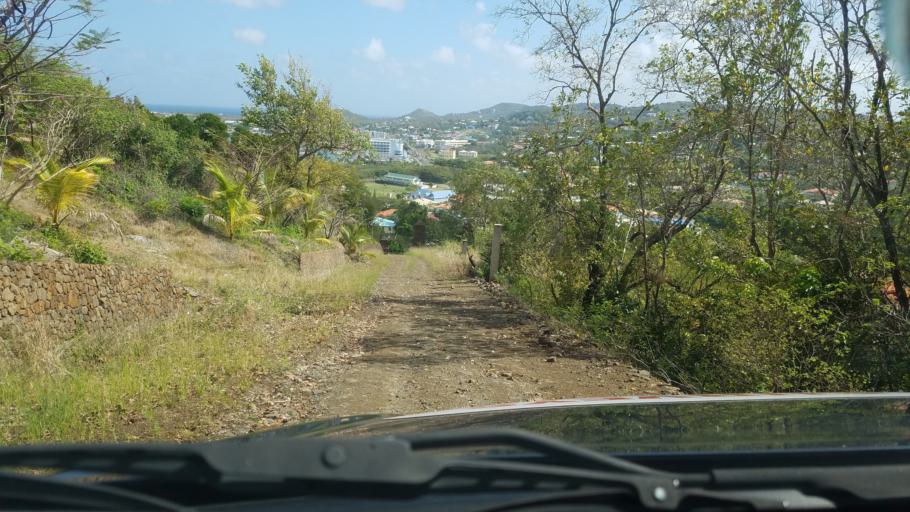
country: LC
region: Gros-Islet
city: Gros Islet
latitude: 14.0649
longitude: -60.9471
